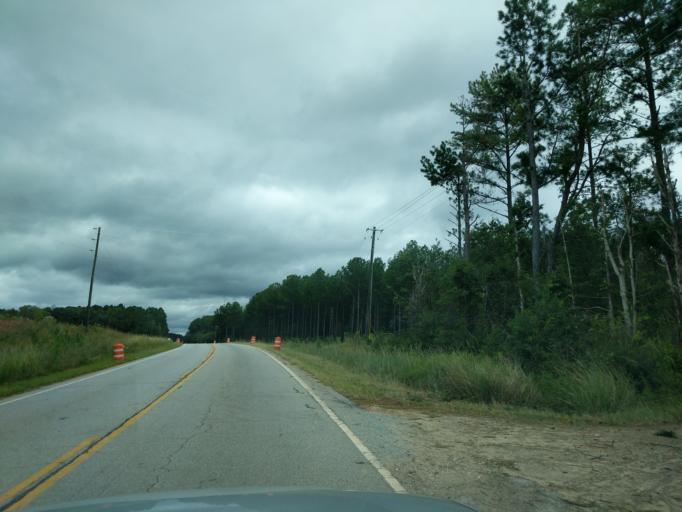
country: US
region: Georgia
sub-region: Wilkes County
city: Washington
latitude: 33.6856
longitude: -82.6436
